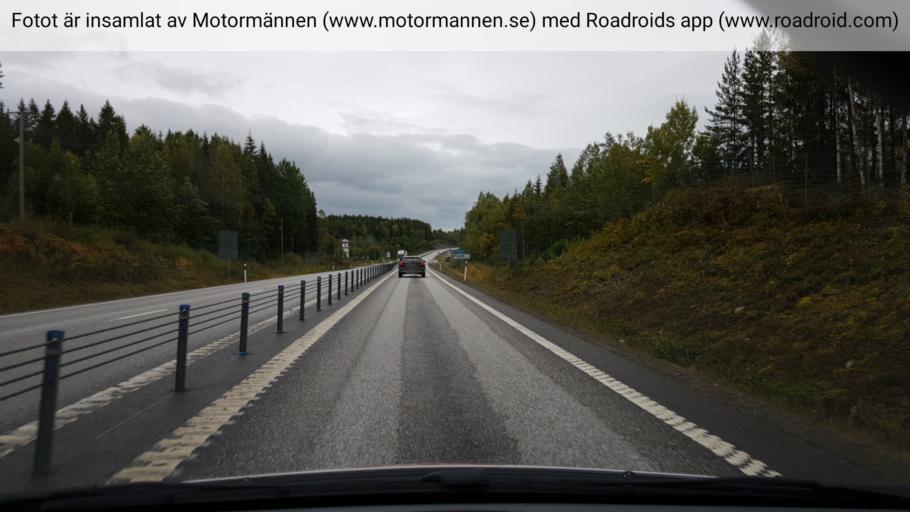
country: SE
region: OErebro
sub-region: Degerfors Kommun
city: Degerfors
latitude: 59.3238
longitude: 14.3655
